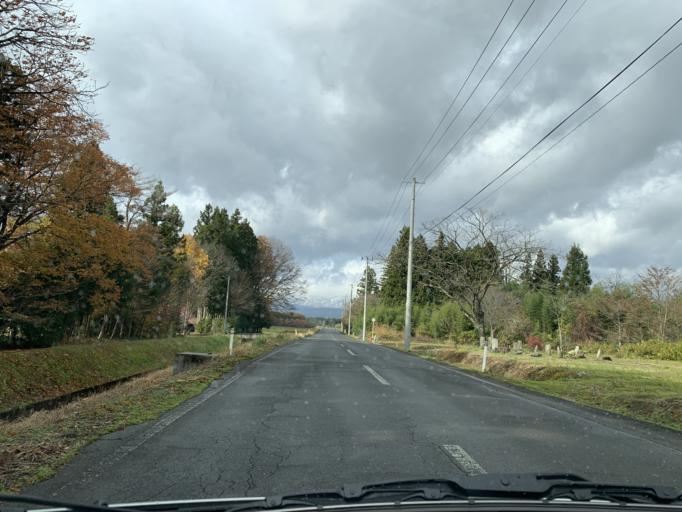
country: JP
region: Iwate
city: Mizusawa
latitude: 39.0916
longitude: 141.0140
